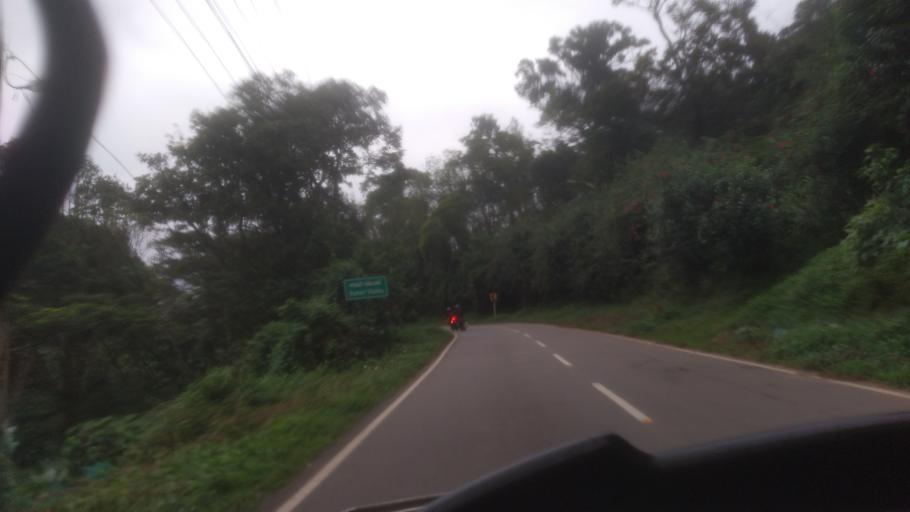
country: IN
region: Tamil Nadu
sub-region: Theni
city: Kombai
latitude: 9.8925
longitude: 77.2032
